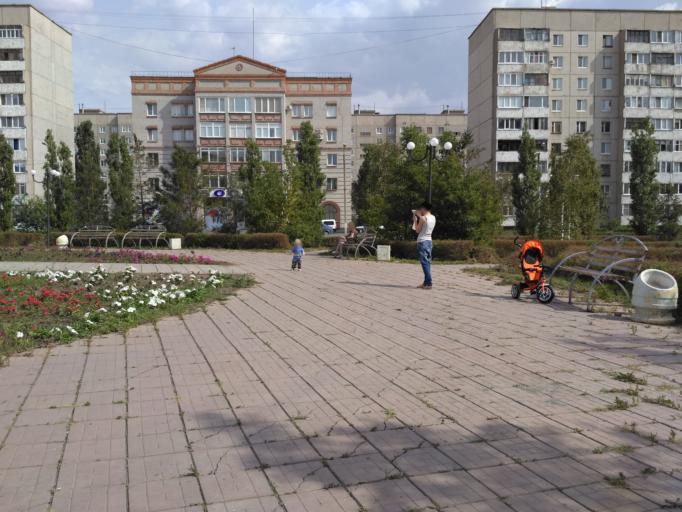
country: RU
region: Orenburg
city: Novotroitsk
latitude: 51.1906
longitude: 58.2811
